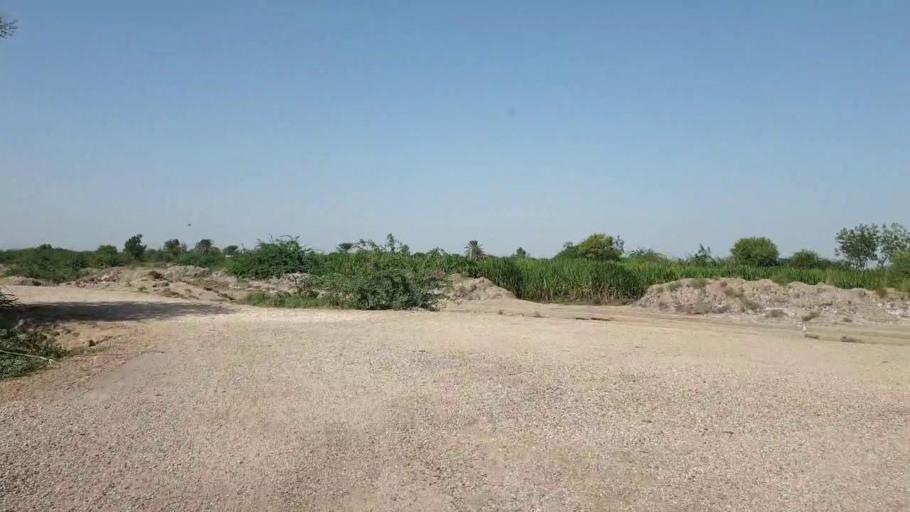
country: PK
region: Sindh
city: Tando Bago
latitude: 24.7421
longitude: 69.0422
